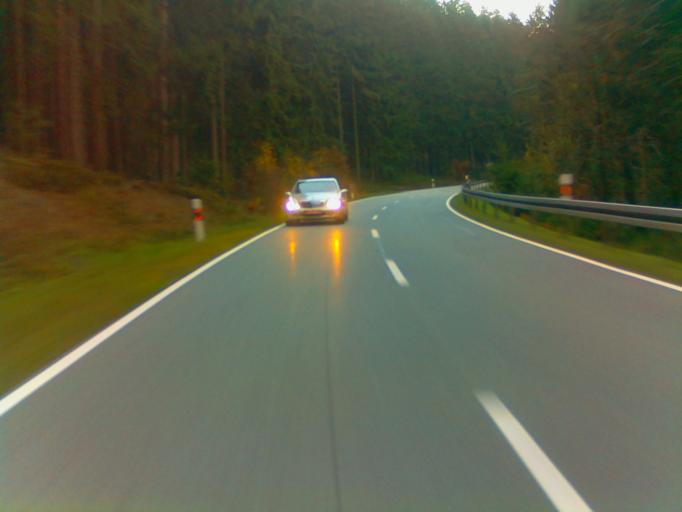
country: DE
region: Hesse
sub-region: Regierungsbezirk Darmstadt
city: Wald-Michelbach
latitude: 49.5974
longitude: 8.8767
